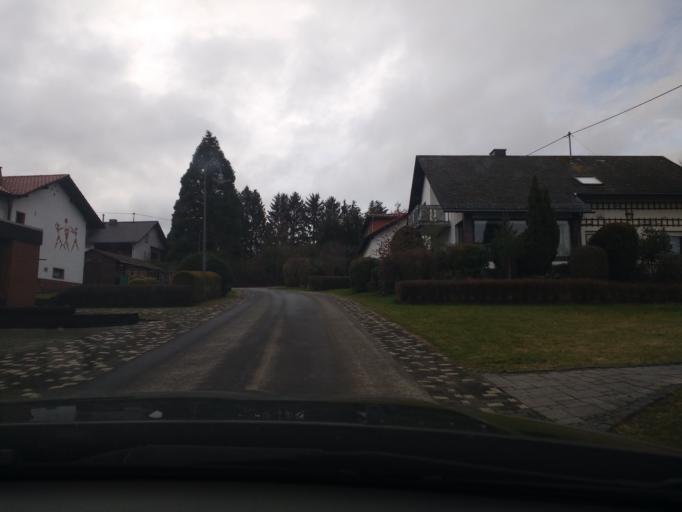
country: DE
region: Rheinland-Pfalz
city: Schillingen
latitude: 49.6373
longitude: 6.7850
